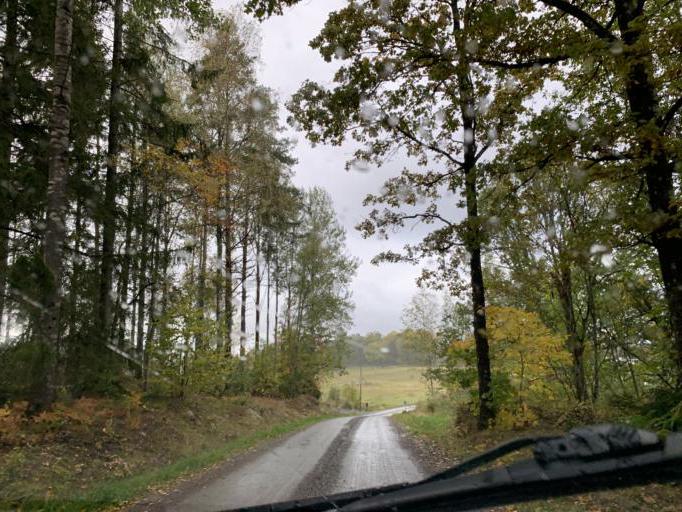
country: SE
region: Soedermanland
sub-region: Eskilstuna Kommun
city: Kvicksund
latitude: 59.3360
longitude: 16.3012
